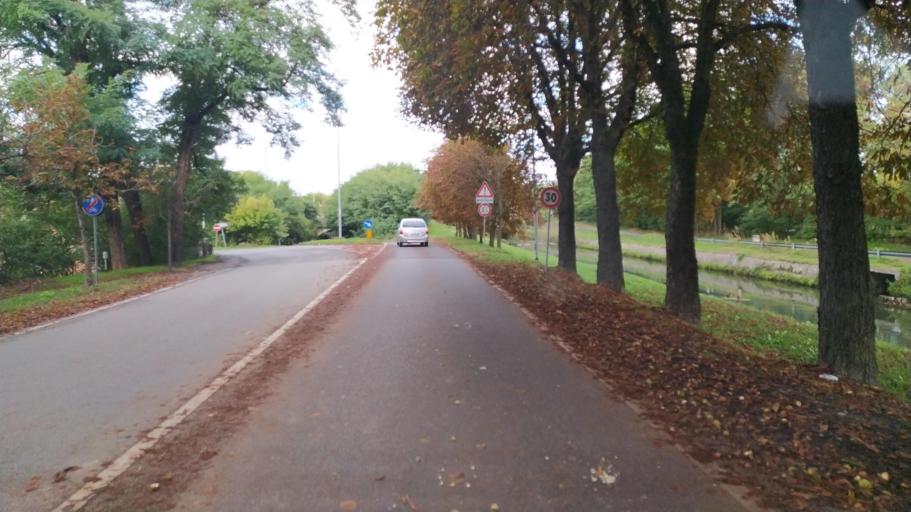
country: IT
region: Lombardy
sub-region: Provincia di Pavia
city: Pavia
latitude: 45.2051
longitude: 9.1508
